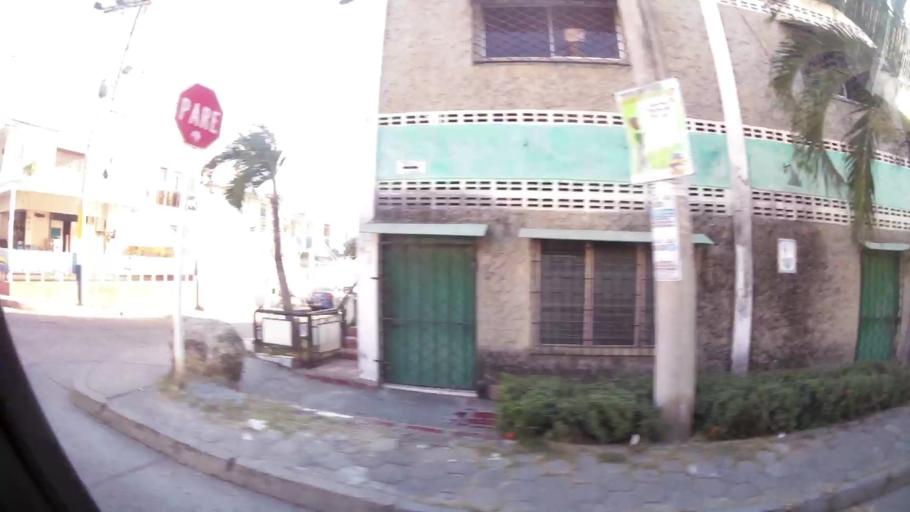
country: CO
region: Bolivar
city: Cartagena
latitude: 10.3970
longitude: -75.4810
